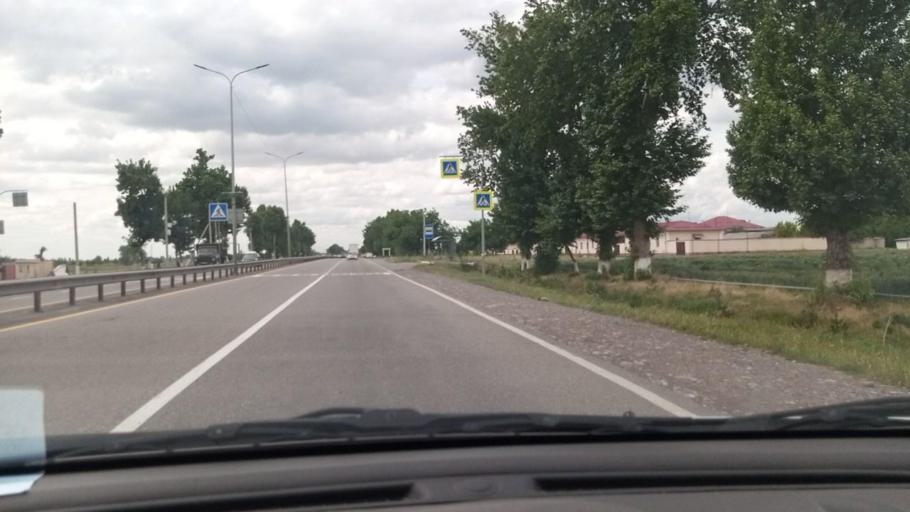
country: UZ
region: Toshkent Shahri
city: Bektemir
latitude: 41.1542
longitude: 69.4251
